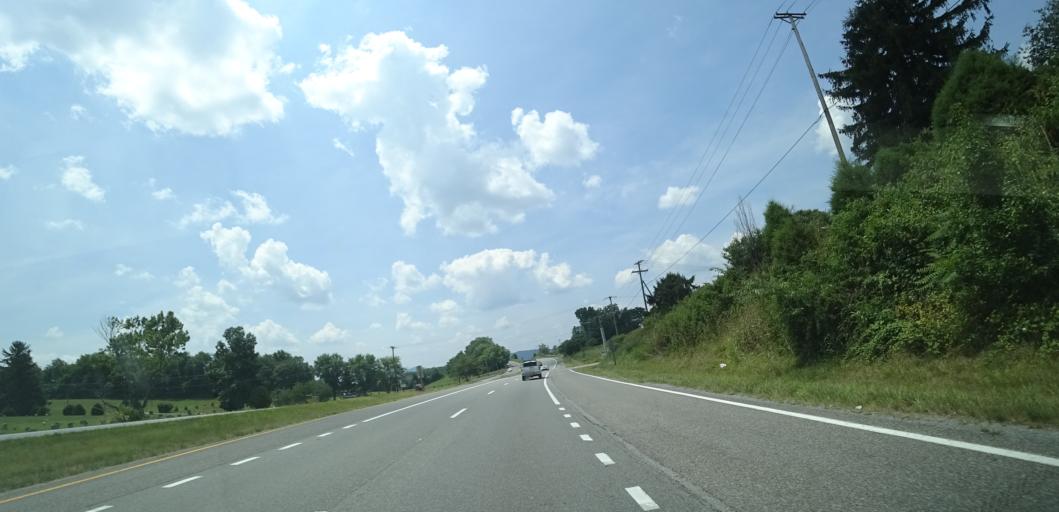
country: US
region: Virginia
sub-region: Botetourt County
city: Daleville
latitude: 37.4530
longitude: -79.8969
